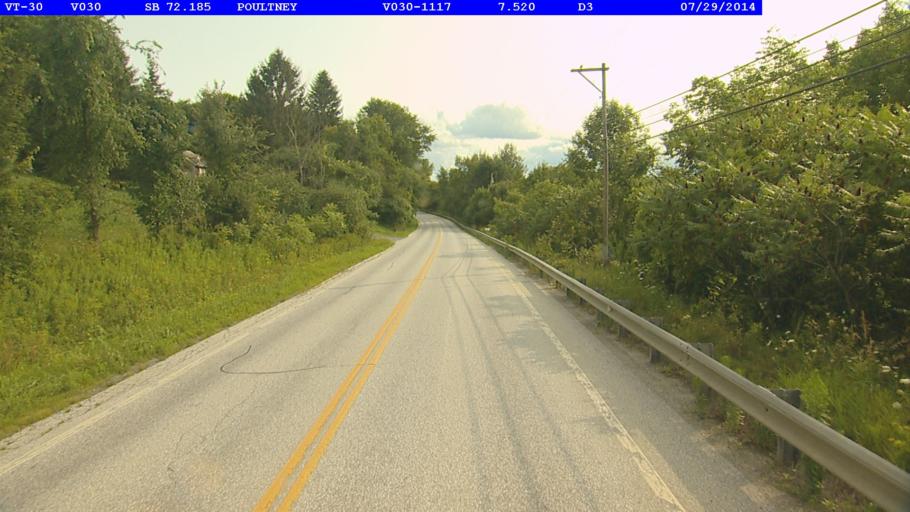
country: US
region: Vermont
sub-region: Rutland County
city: Poultney
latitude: 43.5592
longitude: -73.2261
